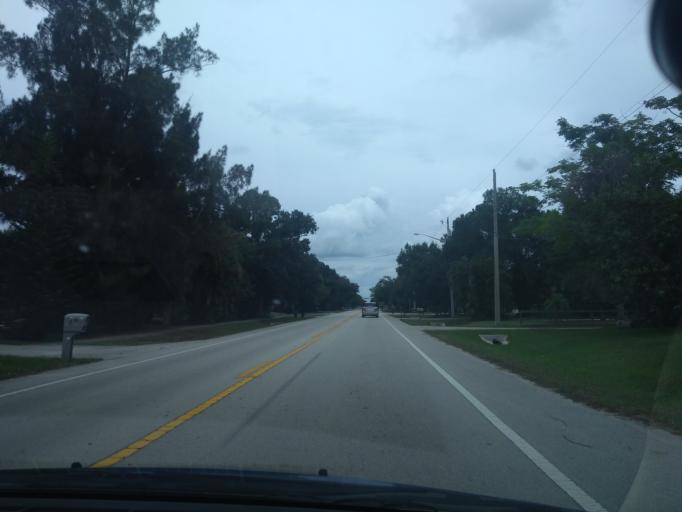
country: US
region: Florida
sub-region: Indian River County
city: Vero Beach South
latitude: 27.6282
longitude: -80.4138
